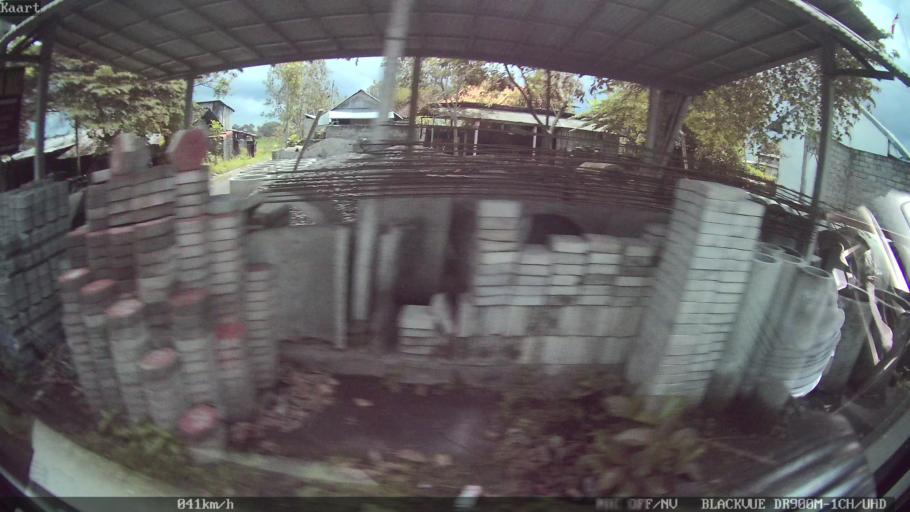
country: ID
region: Bali
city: Banjar Pekenjelodan
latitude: -8.5659
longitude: 115.1846
